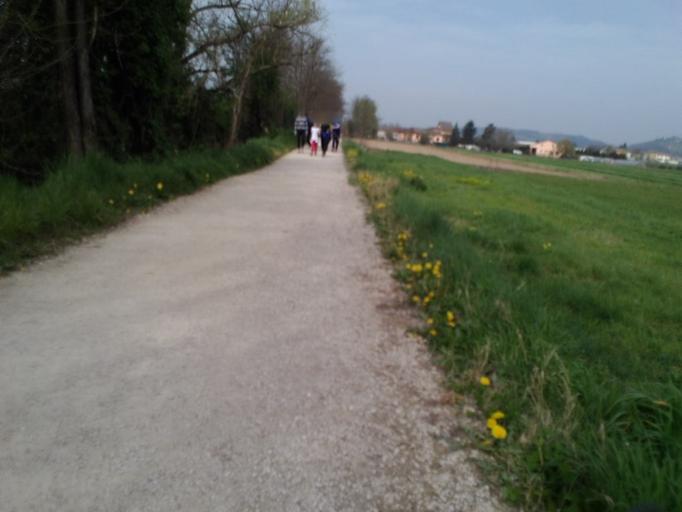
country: IT
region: Veneto
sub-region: Provincia di Verona
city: Rosegaferro
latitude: 45.3548
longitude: 10.8167
